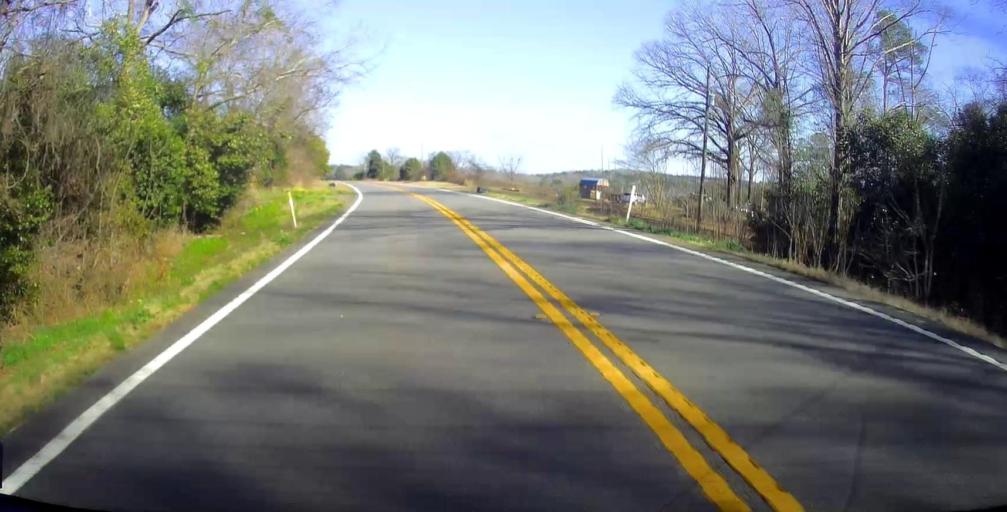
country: US
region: Georgia
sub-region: Macon County
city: Oglethorpe
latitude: 32.3518
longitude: -84.1695
